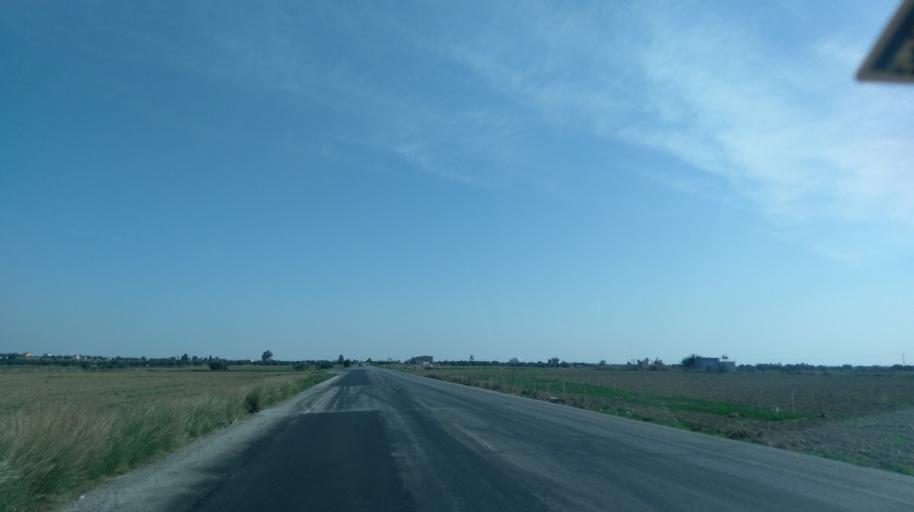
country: CY
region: Larnaka
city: Athienou
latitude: 35.2286
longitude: 33.5374
